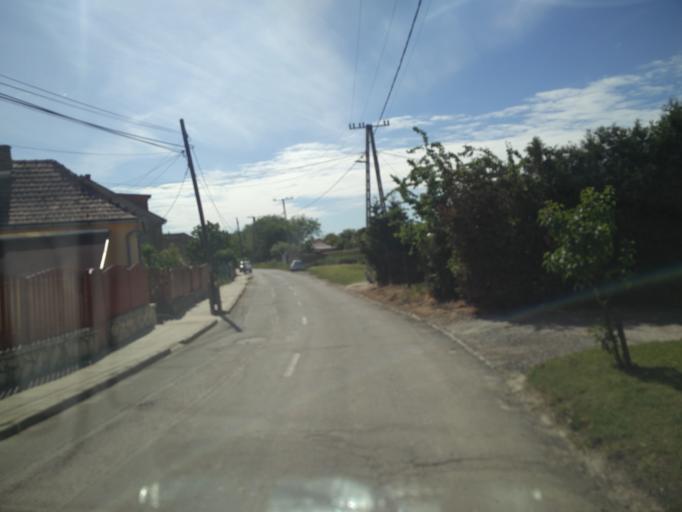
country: HU
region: Tolna
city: Szekszard
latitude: 46.3100
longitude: 18.6847
